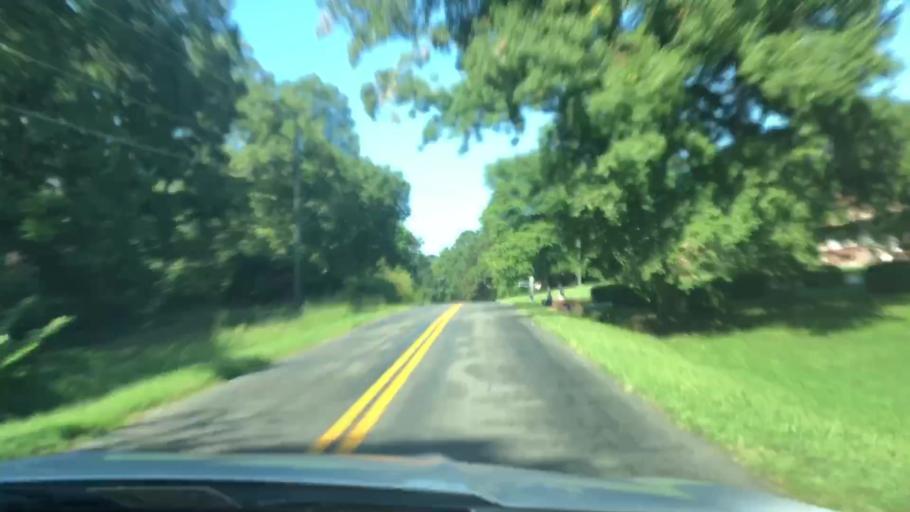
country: US
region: Virginia
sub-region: New Kent County
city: New Kent
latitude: 37.4188
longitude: -76.9209
